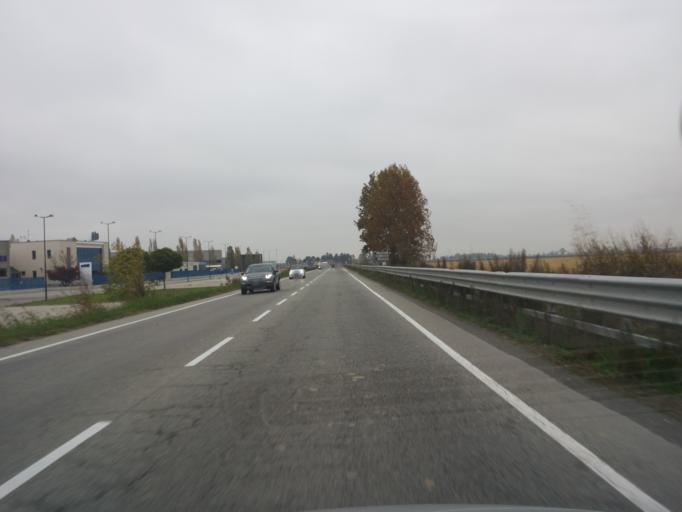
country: IT
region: Piedmont
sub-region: Provincia di Novara
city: Casalino
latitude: 45.3796
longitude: 8.4954
